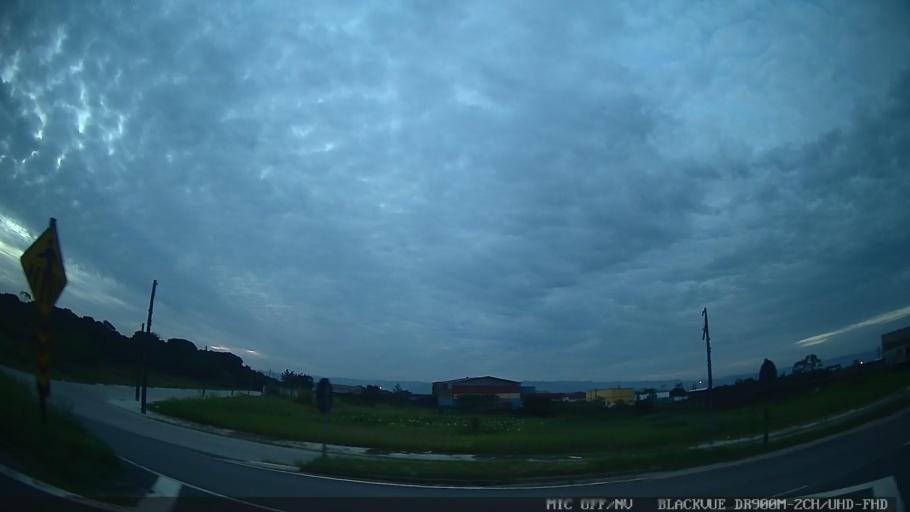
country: BR
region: Sao Paulo
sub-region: Itanhaem
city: Itanhaem
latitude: -24.1920
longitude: -46.8319
